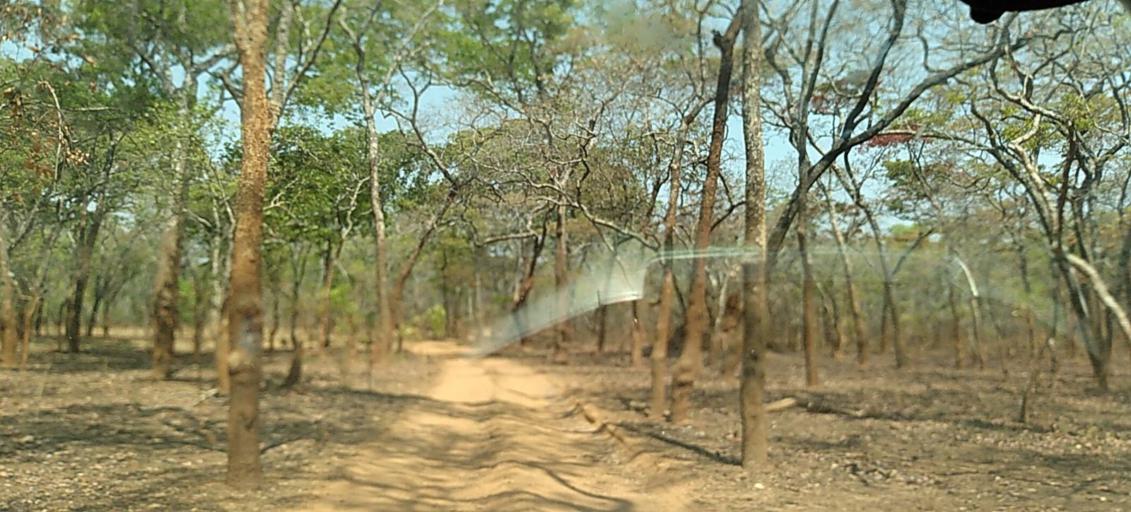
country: ZM
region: North-Western
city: Kasempa
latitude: -13.3937
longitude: 25.5924
